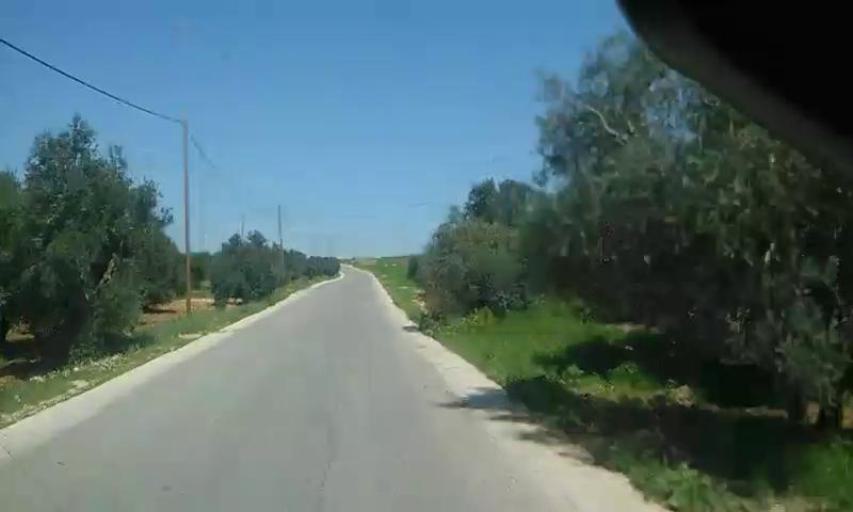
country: PS
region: West Bank
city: Al Majd
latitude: 31.4725
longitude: 34.9483
